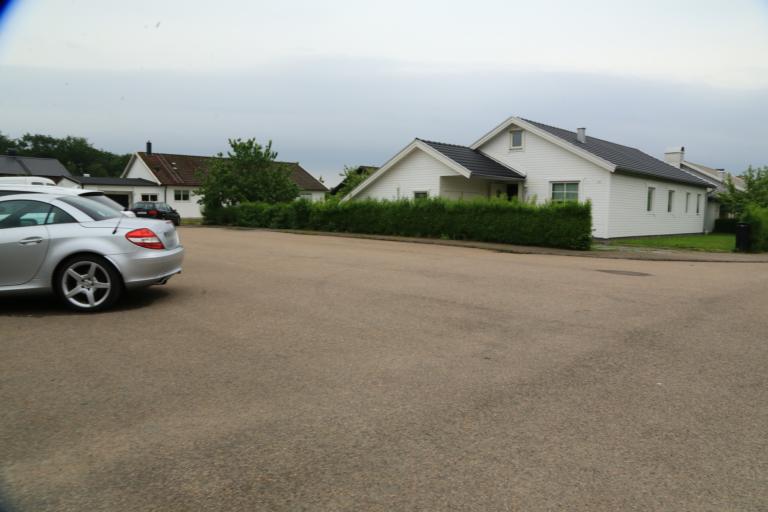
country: SE
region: Halland
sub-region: Varbergs Kommun
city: Varberg
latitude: 57.1045
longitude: 12.2771
